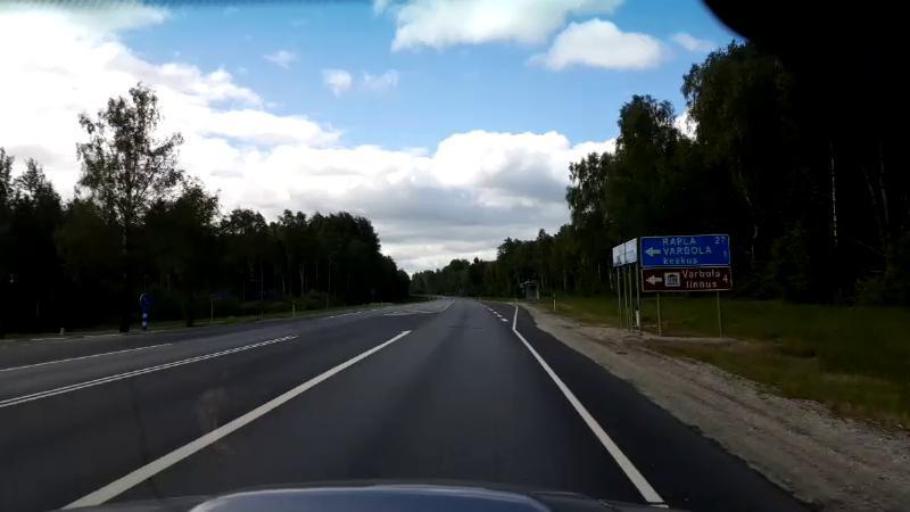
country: EE
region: Raplamaa
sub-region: Maerjamaa vald
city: Marjamaa
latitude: 59.0453
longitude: 24.4432
